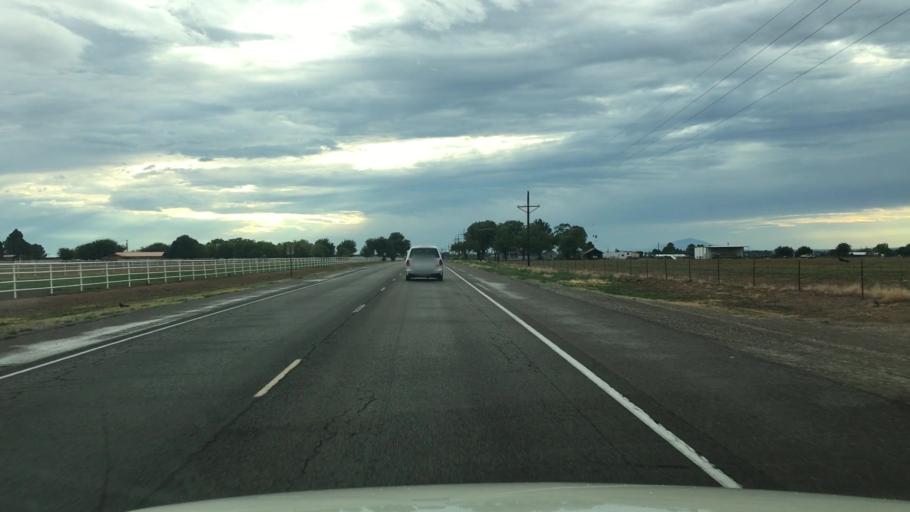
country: US
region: New Mexico
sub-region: Chaves County
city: Roswell
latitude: 33.3944
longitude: -104.4432
